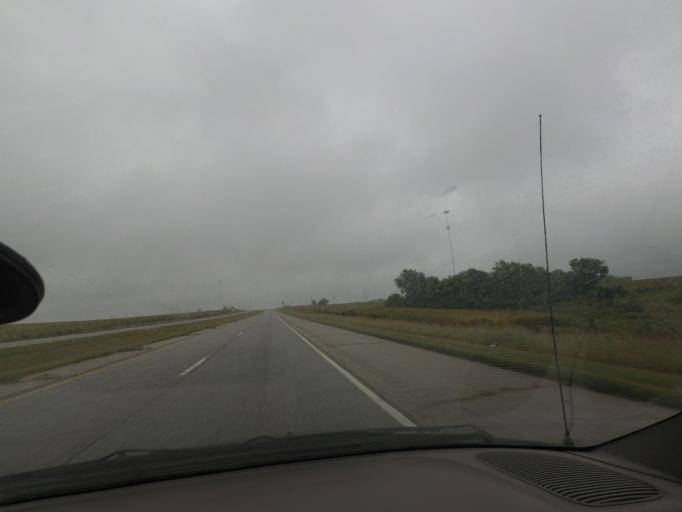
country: US
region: Illinois
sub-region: Pike County
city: Barry
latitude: 39.7005
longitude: -91.0260
